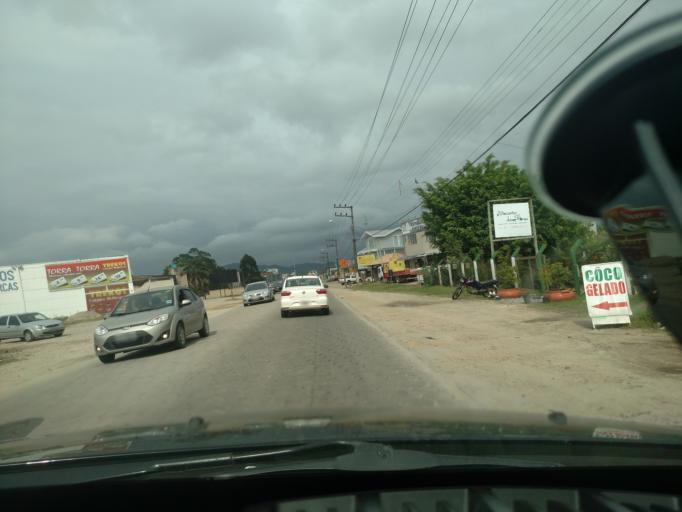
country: BR
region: Santa Catarina
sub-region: Porto Belo
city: Porto Belo
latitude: -27.1582
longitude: -48.5952
